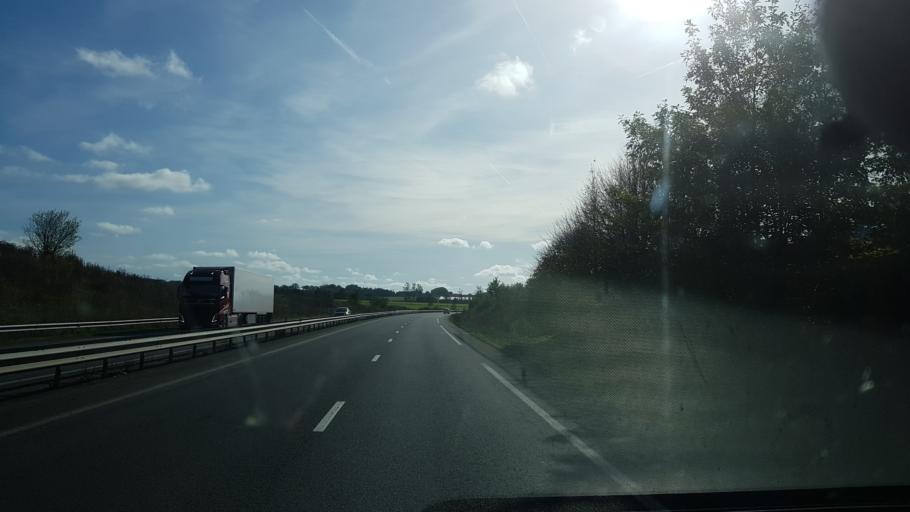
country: FR
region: Poitou-Charentes
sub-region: Departement de la Charente
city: Chasseneuil-sur-Bonnieure
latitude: 45.8212
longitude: 0.4566
